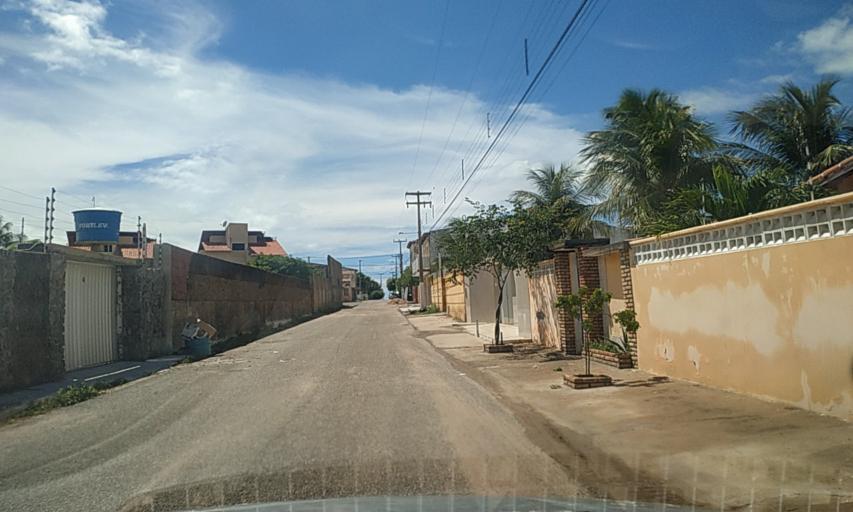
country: BR
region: Rio Grande do Norte
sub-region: Areia Branca
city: Areia Branca
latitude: -4.9291
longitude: -37.1154
